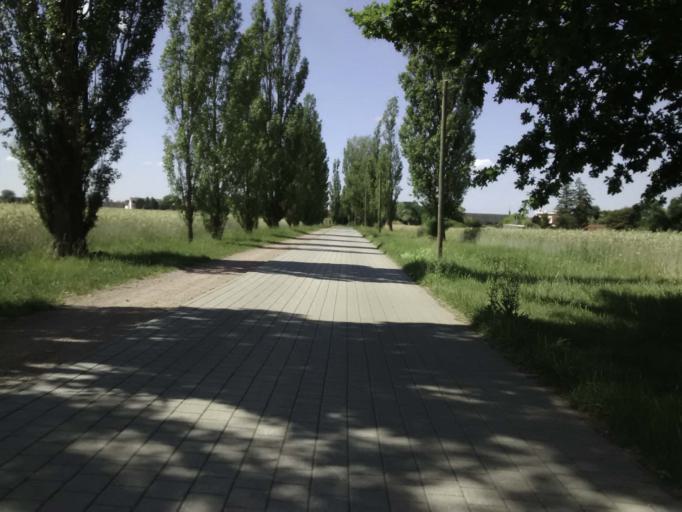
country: DE
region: Saxony-Anhalt
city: Worlitz
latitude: 51.8428
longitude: 12.4345
